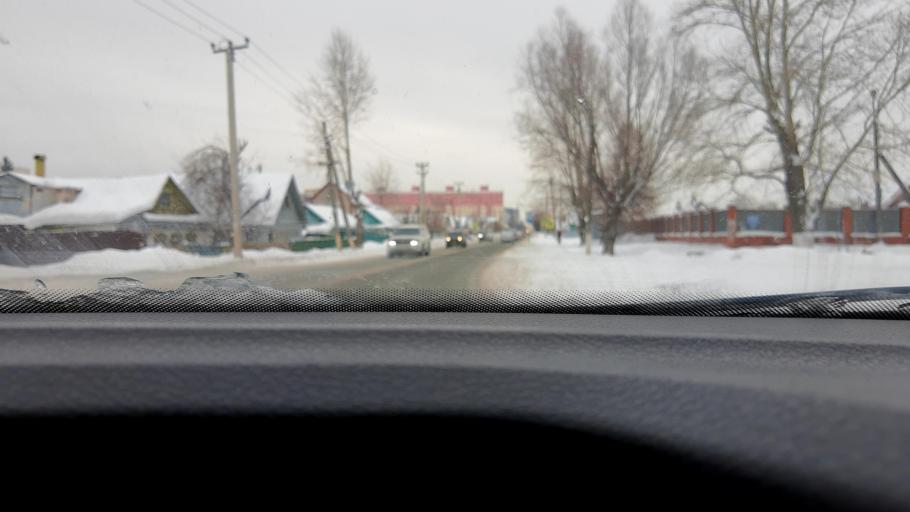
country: RU
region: Bashkortostan
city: Avdon
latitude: 54.7118
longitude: 55.8156
